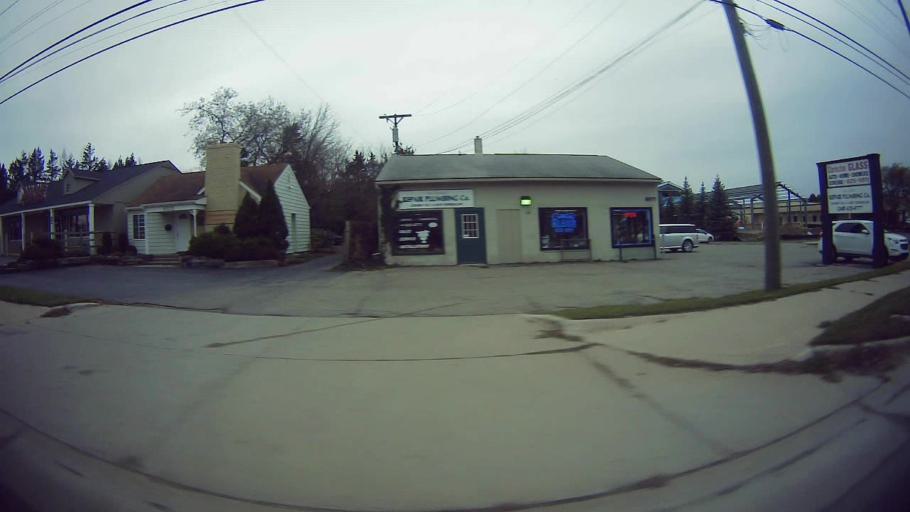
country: US
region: Michigan
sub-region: Oakland County
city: Clarkston
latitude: 42.7158
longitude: -83.4128
